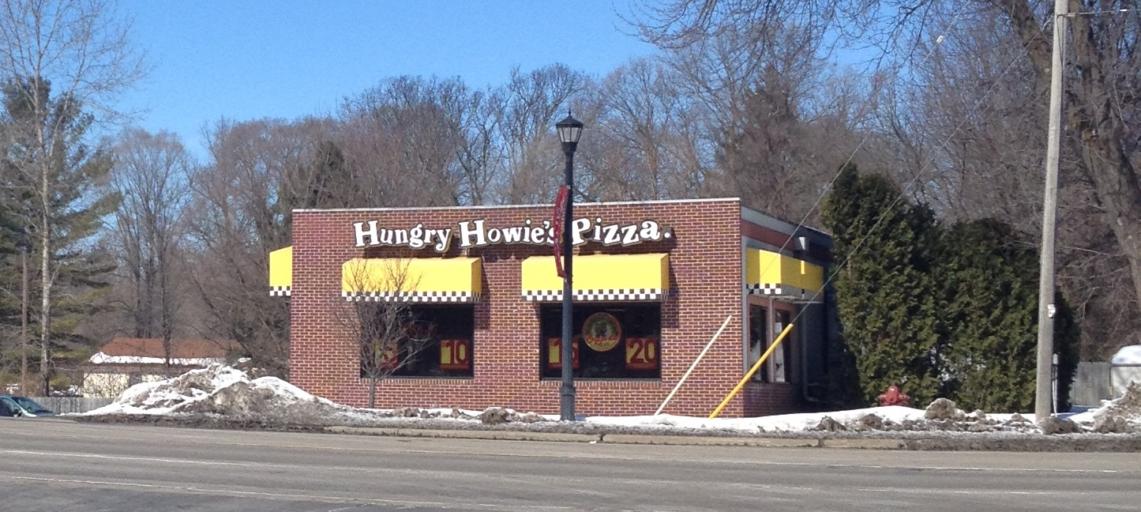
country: US
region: Michigan
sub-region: Gladwin County
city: Gladwin
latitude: 43.9806
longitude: -84.4953
